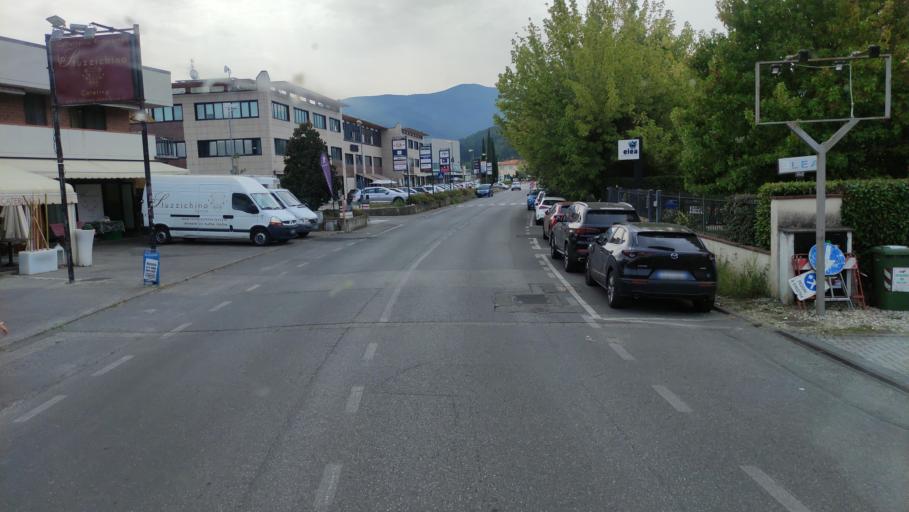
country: IT
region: Tuscany
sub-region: Provincia di Lucca
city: Lucca
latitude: 43.8129
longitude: 10.4979
